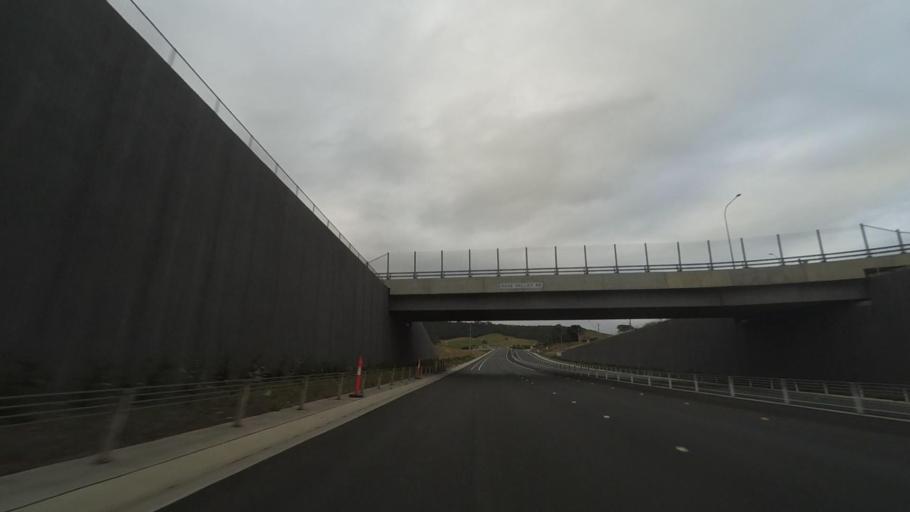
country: AU
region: New South Wales
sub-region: Kiama
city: Gerringong
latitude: -34.7238
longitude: 150.8290
